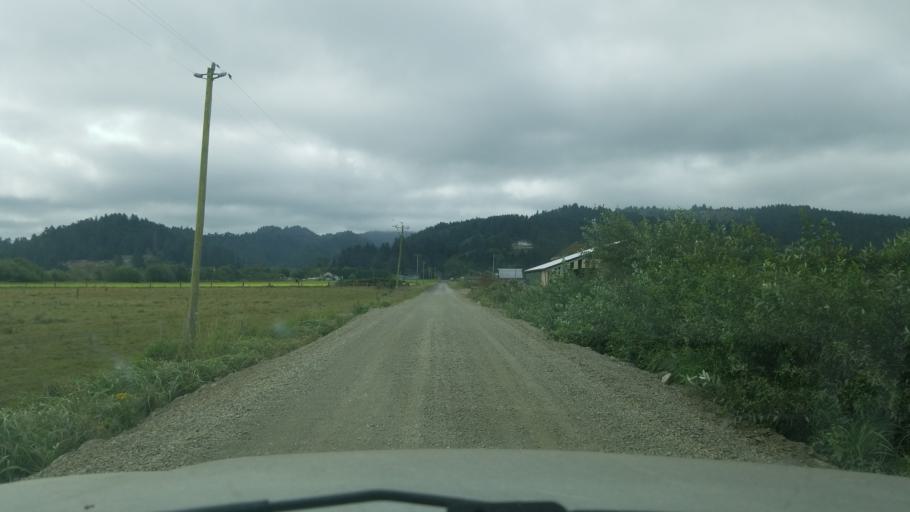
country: US
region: California
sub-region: Humboldt County
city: Ferndale
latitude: 40.5904
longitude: -124.2840
